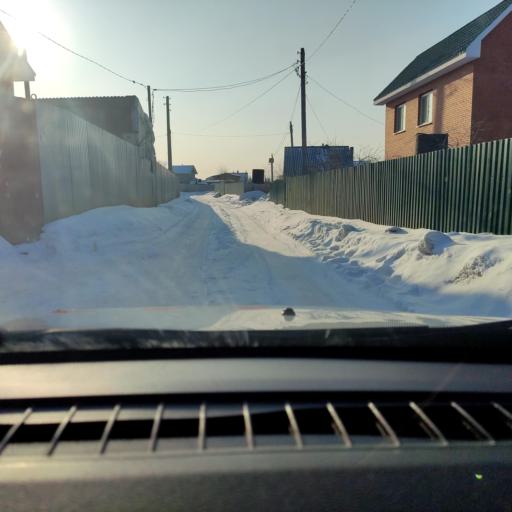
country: RU
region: Samara
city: Samara
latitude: 53.1309
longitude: 50.2473
